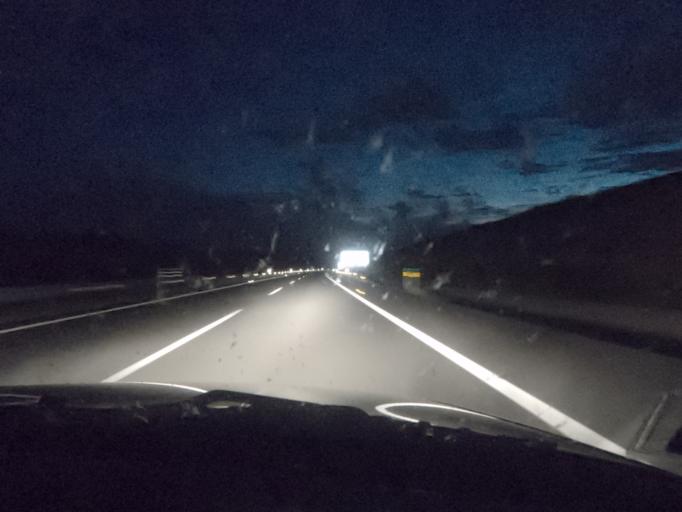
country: ES
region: Extremadura
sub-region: Provincia de Caceres
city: Coria
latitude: 39.9864
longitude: -6.4810
